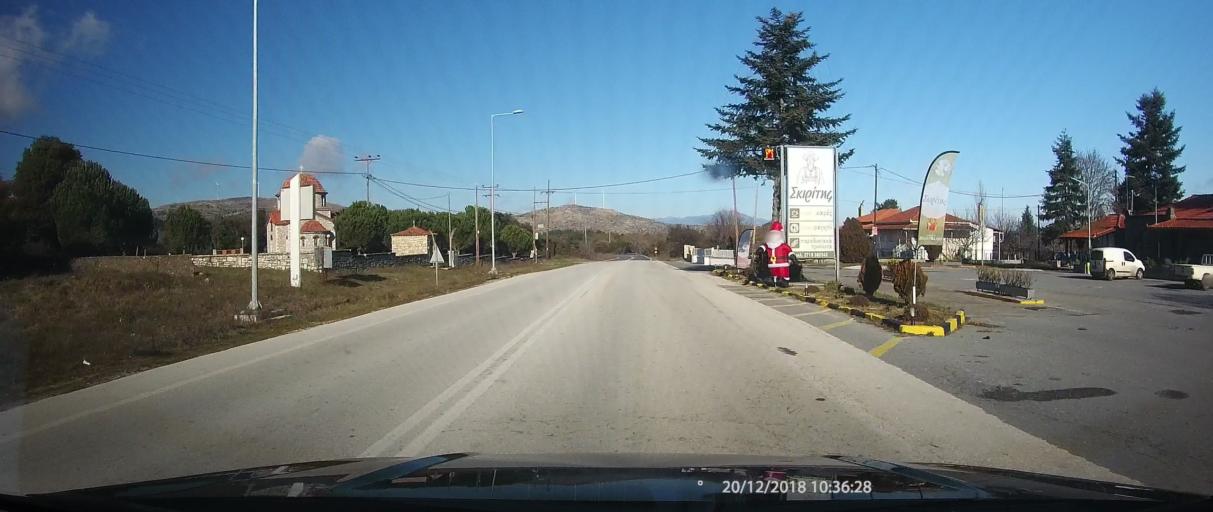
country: GR
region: Peloponnese
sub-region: Nomos Lakonias
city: Kariai
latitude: 37.3666
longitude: 22.4012
